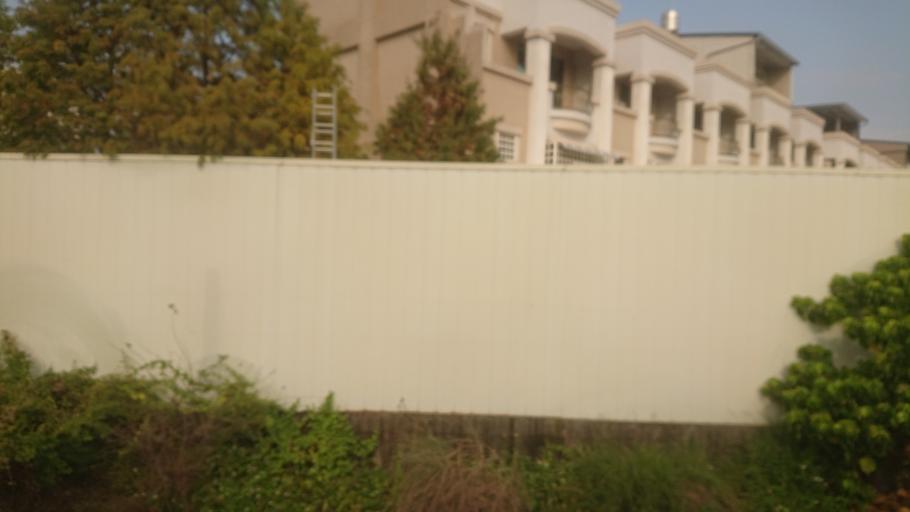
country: TW
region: Taiwan
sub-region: Yunlin
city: Douliu
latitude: 23.7064
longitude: 120.5330
